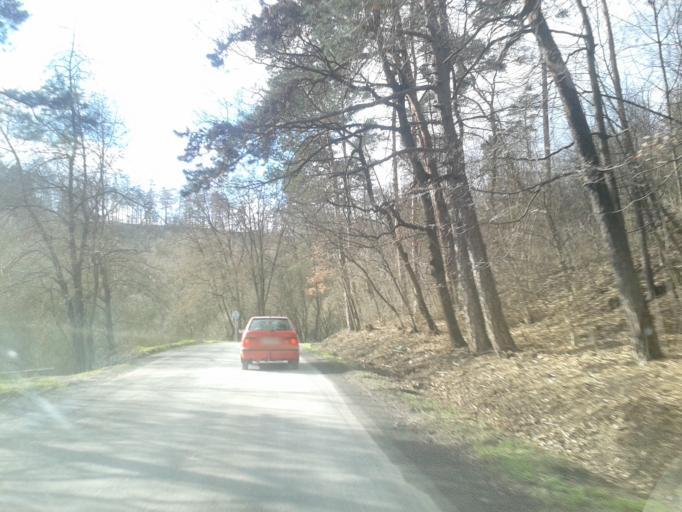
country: CZ
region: Central Bohemia
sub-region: Okres Beroun
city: Beroun
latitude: 49.9071
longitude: 14.1117
